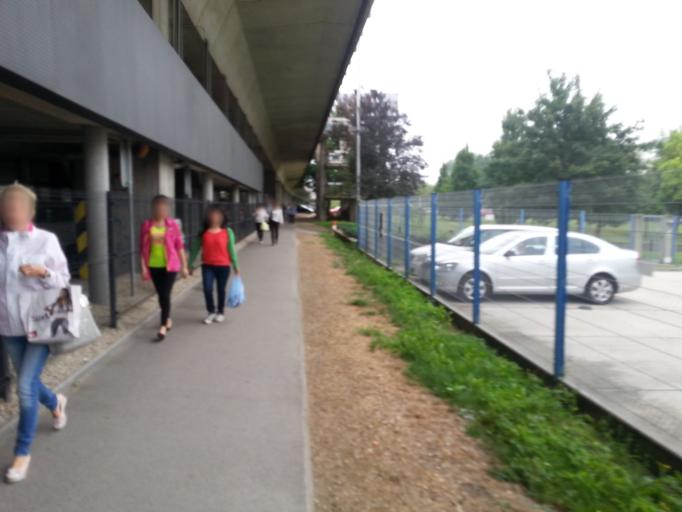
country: SK
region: Bratislavsky
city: Bratislava
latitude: 48.1289
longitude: 17.1049
